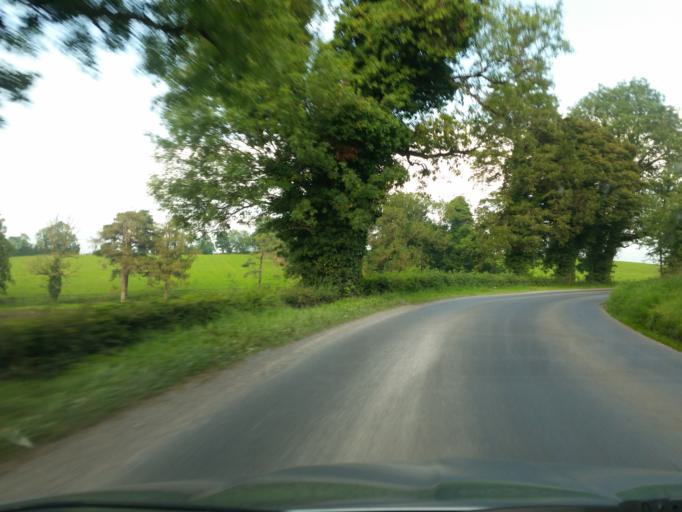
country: GB
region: Northern Ireland
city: Fivemiletown
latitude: 54.3758
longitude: -7.3670
